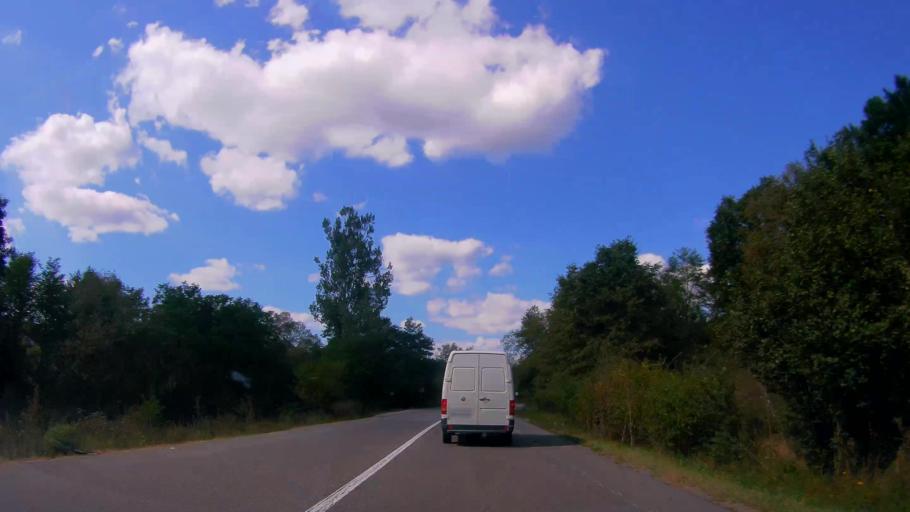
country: RO
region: Salaj
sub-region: Comuna Romanasi
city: Romanasi
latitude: 47.1106
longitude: 23.1661
